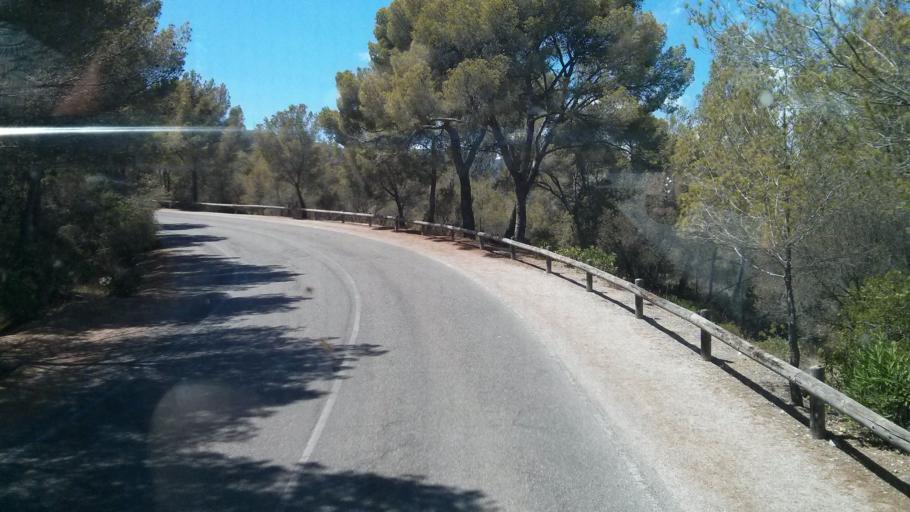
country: ES
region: Balearic Islands
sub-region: Illes Balears
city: Palma
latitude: 39.5671
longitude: 2.6171
